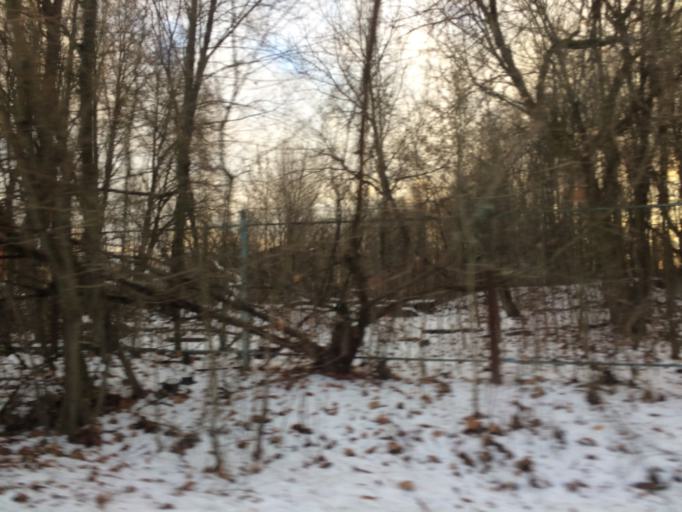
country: RU
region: Tula
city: Cherepet'
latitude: 54.1172
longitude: 36.3366
